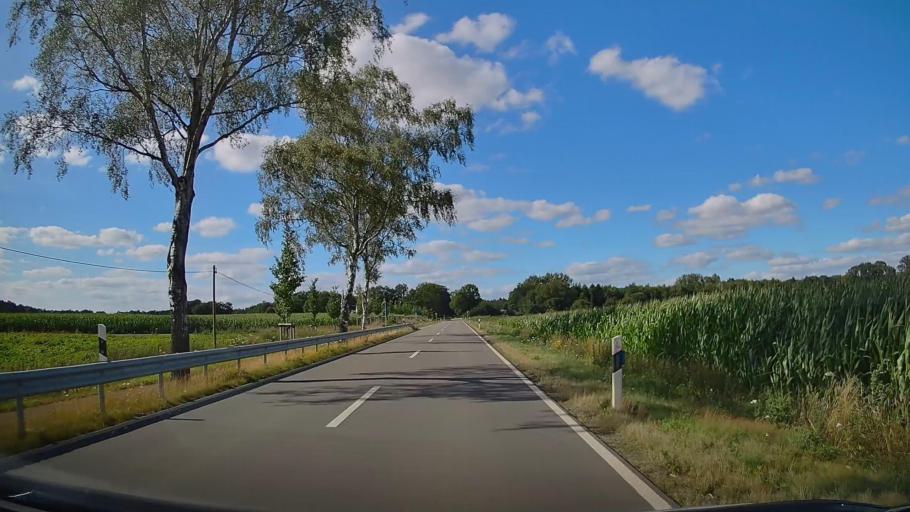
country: DE
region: Lower Saxony
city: Loningen
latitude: 52.7018
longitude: 7.7582
